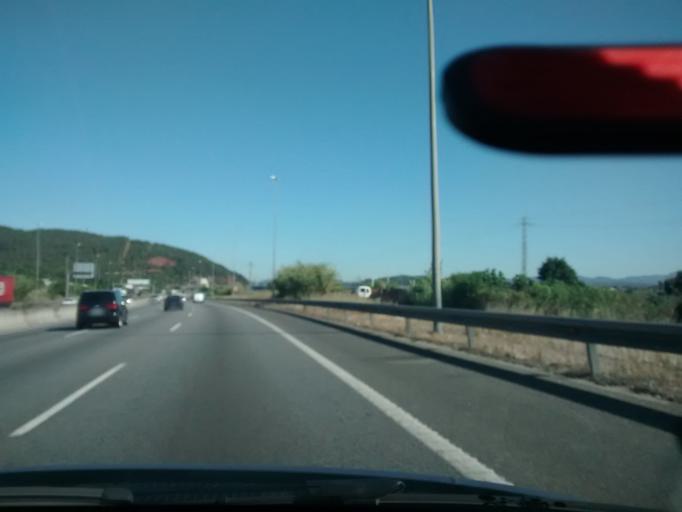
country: ES
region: Catalonia
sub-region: Provincia de Barcelona
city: Palleja
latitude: 41.4271
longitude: 2.0002
